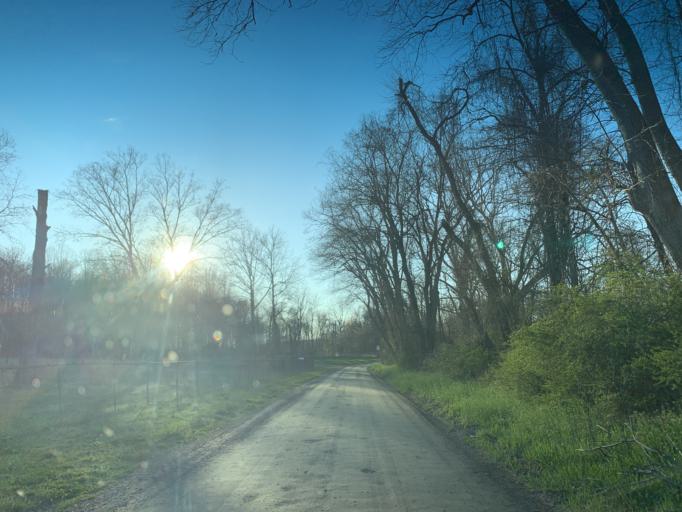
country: US
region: Maryland
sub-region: Harford County
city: South Bel Air
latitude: 39.6006
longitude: -76.2580
